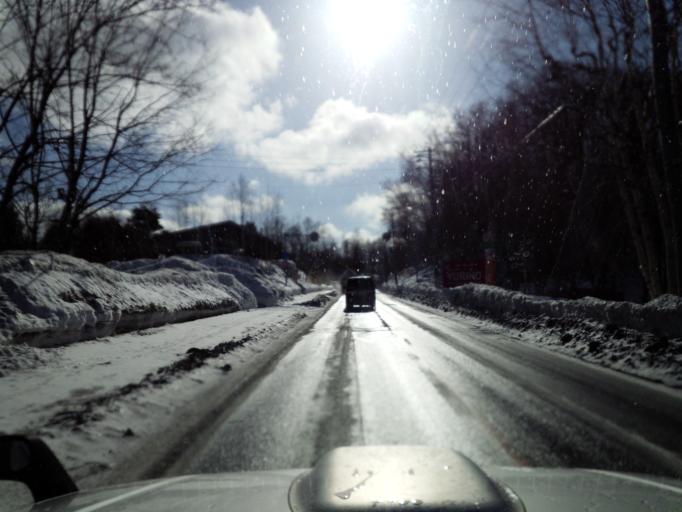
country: JP
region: Hokkaido
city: Sapporo
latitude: 42.9325
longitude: 141.3431
